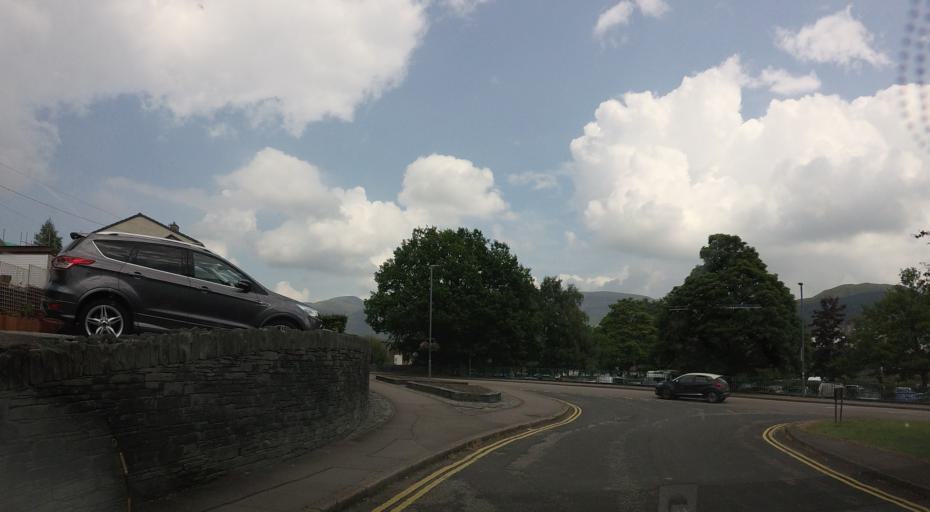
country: GB
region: England
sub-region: Cumbria
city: Keswick
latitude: 54.5993
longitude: -3.1389
